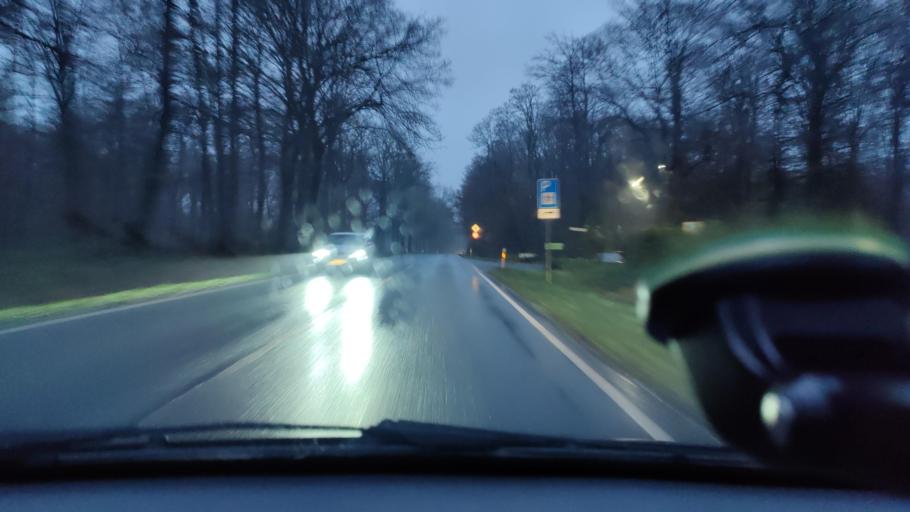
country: DE
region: North Rhine-Westphalia
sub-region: Regierungsbezirk Dusseldorf
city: Sonsbeck
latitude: 51.5892
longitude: 6.3859
